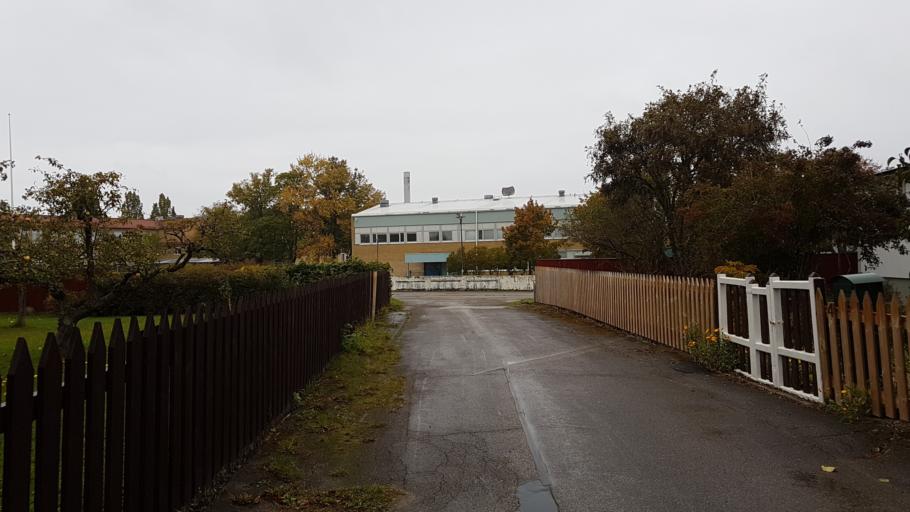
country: SE
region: Gotland
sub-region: Gotland
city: Visby
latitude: 57.6237
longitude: 18.2875
